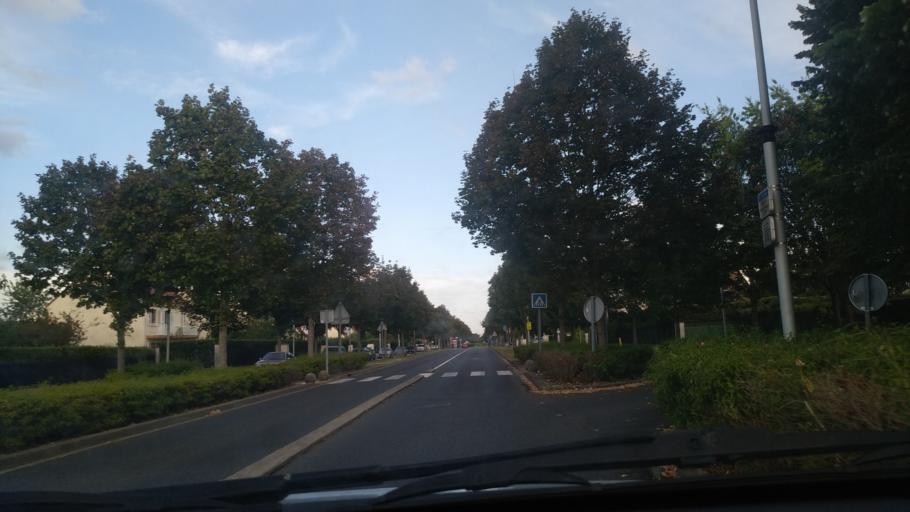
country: FR
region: Ile-de-France
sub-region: Departement de Seine-et-Marne
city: Lieusaint
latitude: 48.6379
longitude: 2.5498
